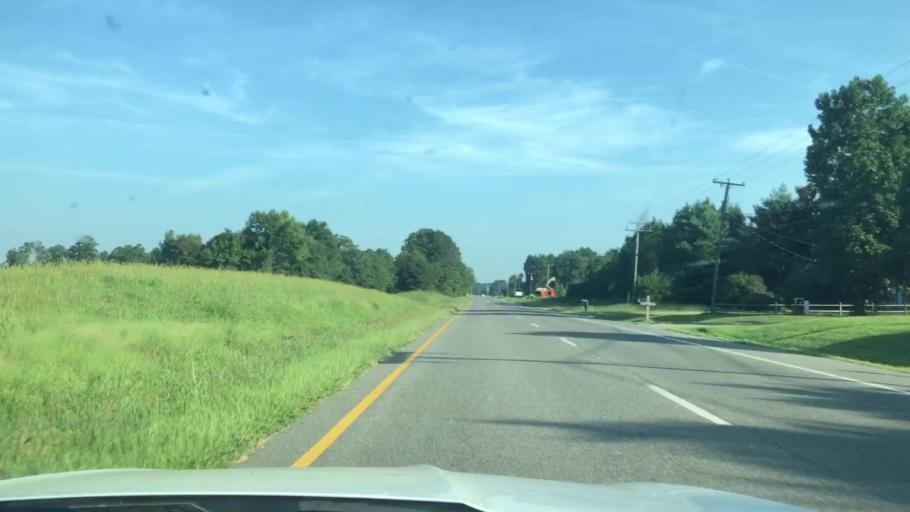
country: US
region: Virginia
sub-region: Middlesex County
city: Saluda
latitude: 37.7068
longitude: -76.6898
